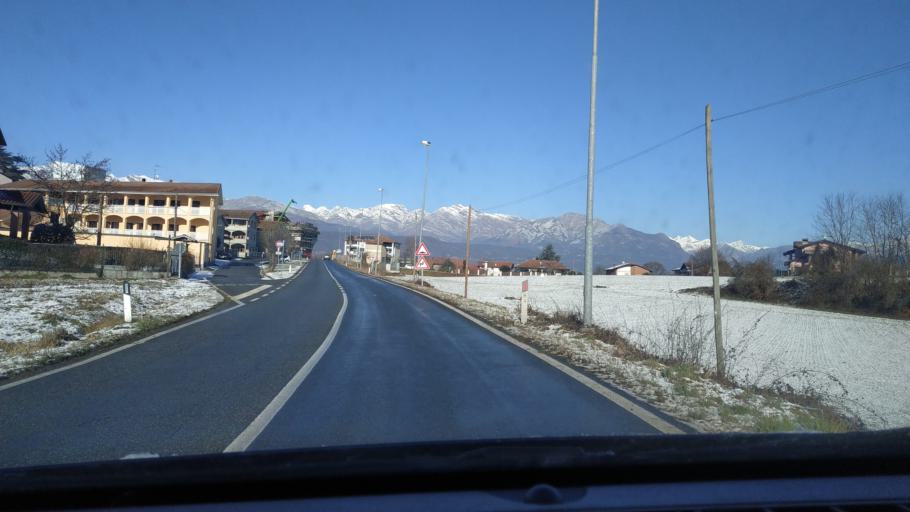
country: IT
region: Piedmont
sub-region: Provincia di Torino
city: Perosa Canavese
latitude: 45.3940
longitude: 7.8341
